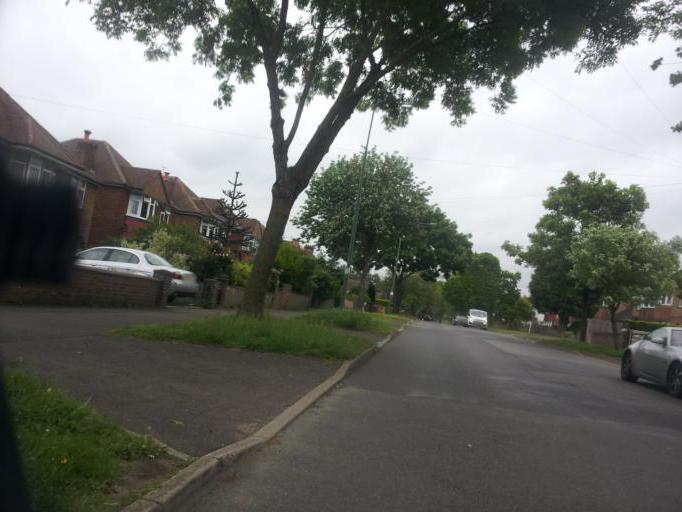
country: GB
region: England
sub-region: Kent
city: Maidstone
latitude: 51.2620
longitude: 0.5313
